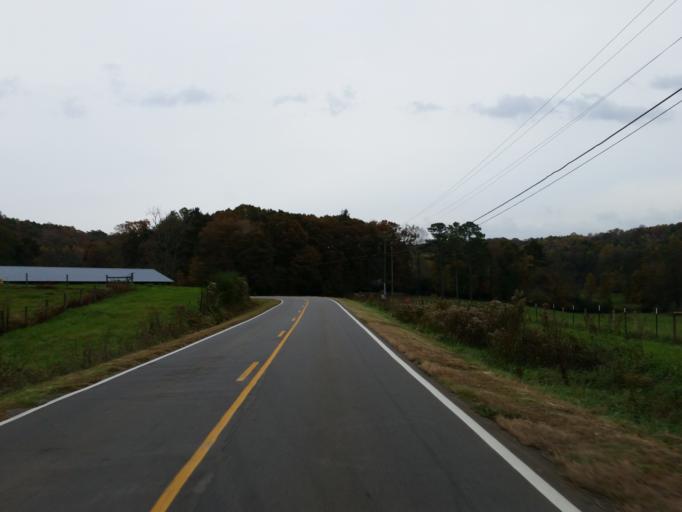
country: US
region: Georgia
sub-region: Gilmer County
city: Ellijay
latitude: 34.6564
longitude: -84.3585
